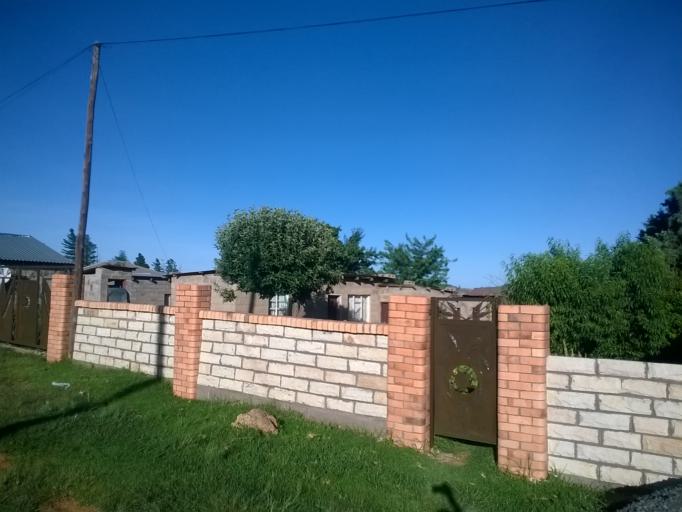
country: LS
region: Maseru
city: Maseru
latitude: -29.2889
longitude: 27.5281
